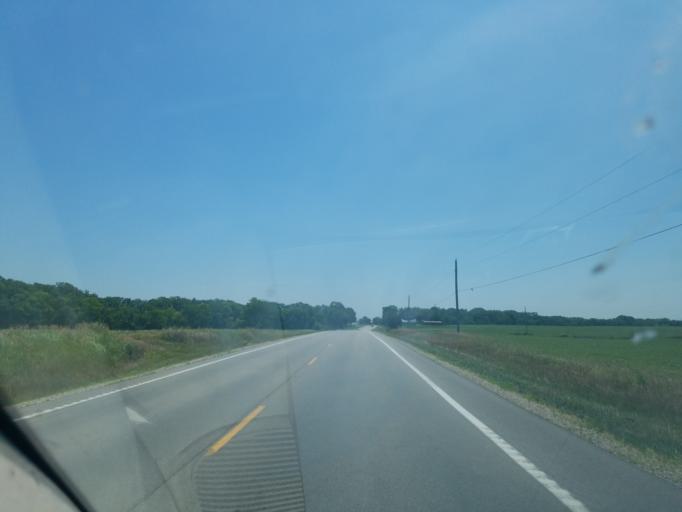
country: US
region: Ohio
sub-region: Mercer County
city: Rockford
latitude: 40.7293
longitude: -84.7455
